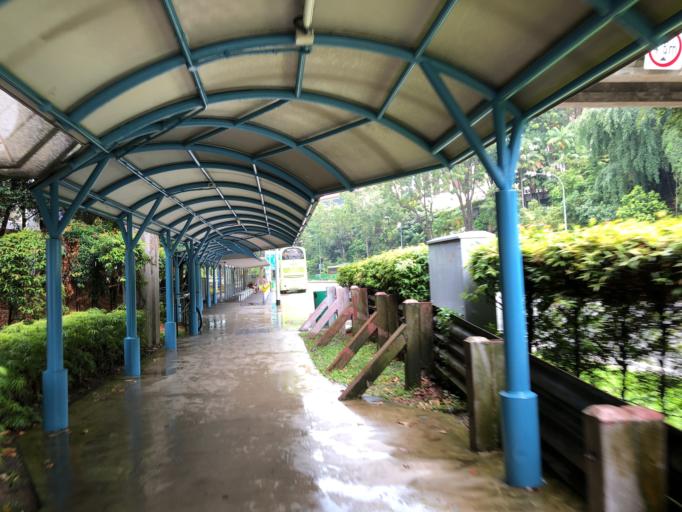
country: MY
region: Johor
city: Johor Bahru
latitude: 1.3512
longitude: 103.7502
